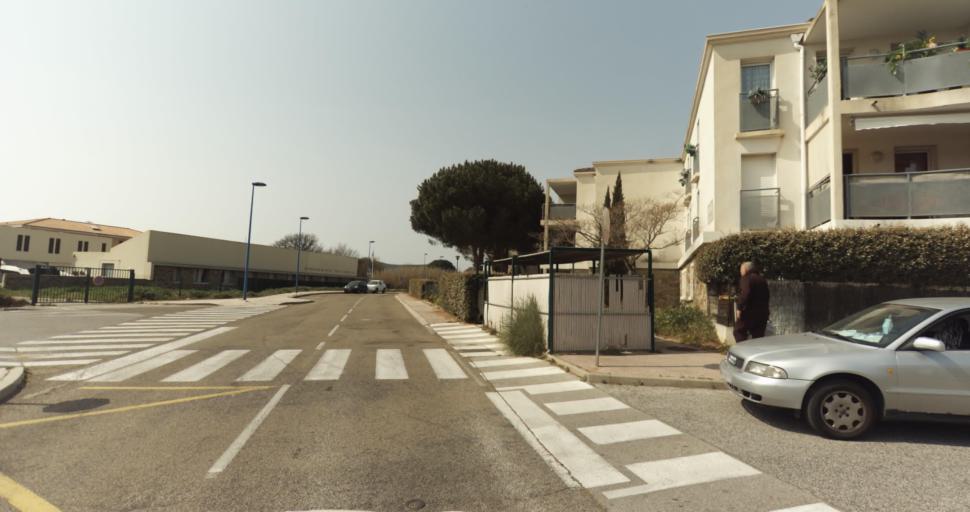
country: FR
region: Provence-Alpes-Cote d'Azur
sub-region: Departement du Var
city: Bormes-les-Mimosas
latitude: 43.1384
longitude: 6.3474
